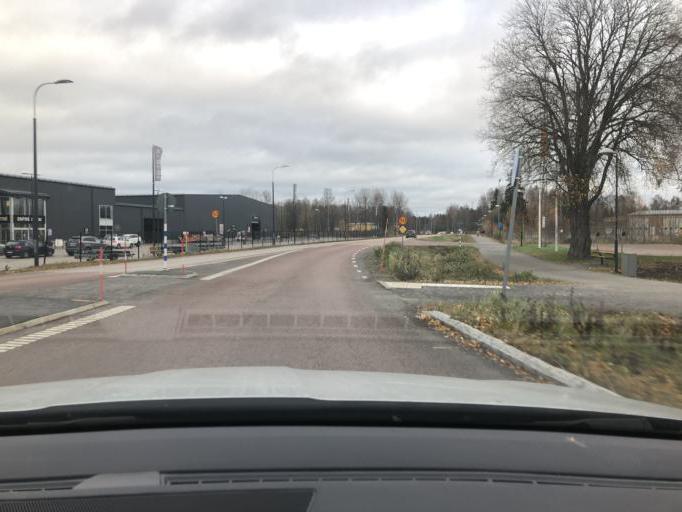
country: SE
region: Uppsala
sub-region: Tierps Kommun
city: Tierp
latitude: 60.3460
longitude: 17.4916
